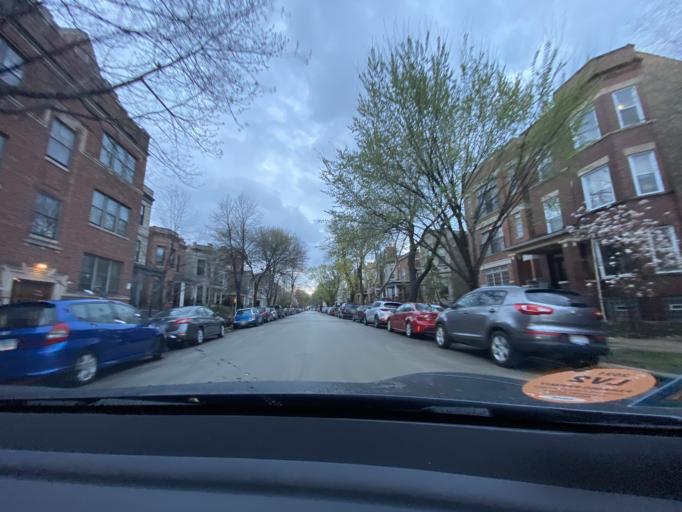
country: US
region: Illinois
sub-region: Cook County
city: Lincolnwood
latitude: 41.9491
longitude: -87.6629
